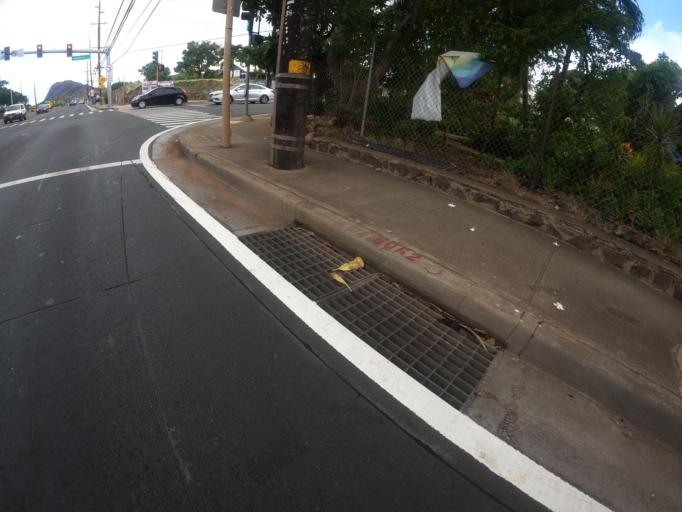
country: US
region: Hawaii
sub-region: Honolulu County
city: Nanakuli
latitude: 21.3786
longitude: -158.1423
